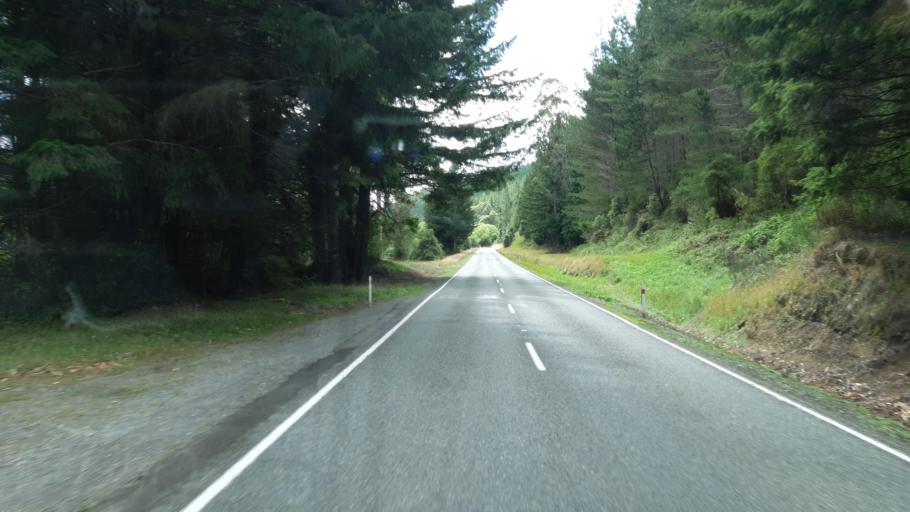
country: NZ
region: Tasman
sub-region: Tasman District
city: Wakefield
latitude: -41.6004
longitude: 172.7596
